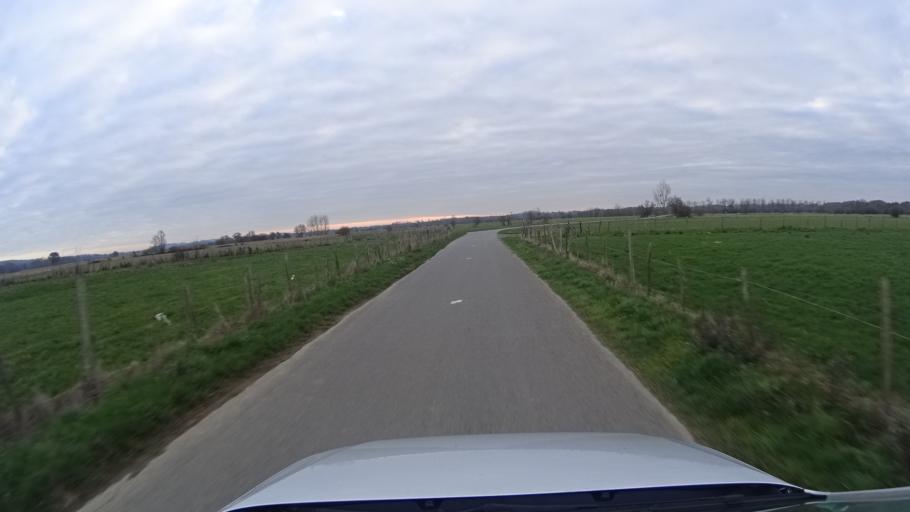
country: FR
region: Pays de la Loire
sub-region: Departement de la Loire-Atlantique
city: Avessac
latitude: 47.6868
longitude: -1.9256
